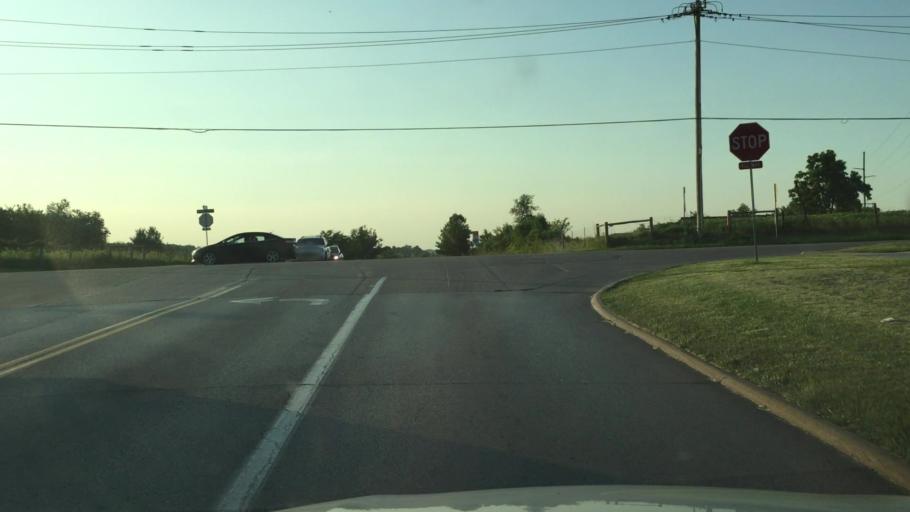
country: US
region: Iowa
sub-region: Johnson County
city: Iowa City
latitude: 41.6685
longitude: -91.4834
